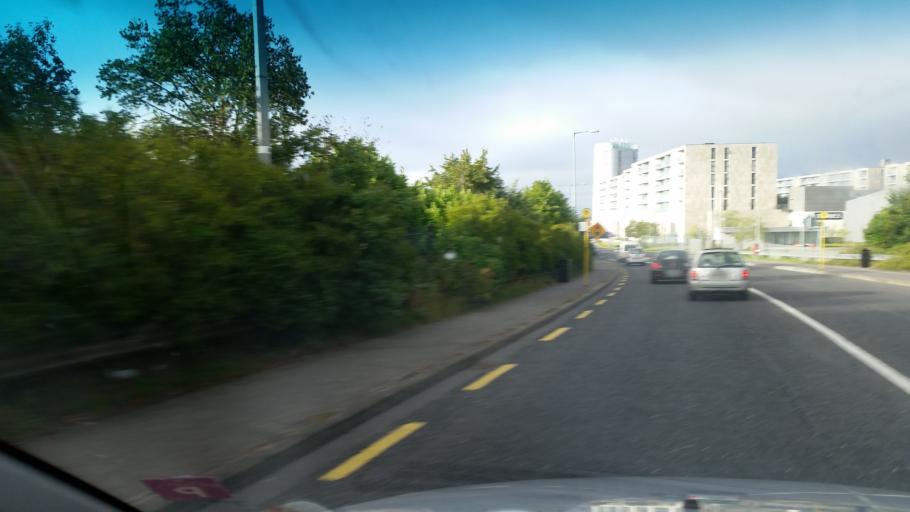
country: IE
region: Leinster
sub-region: Dublin City
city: Finglas
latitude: 53.4059
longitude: -6.3005
